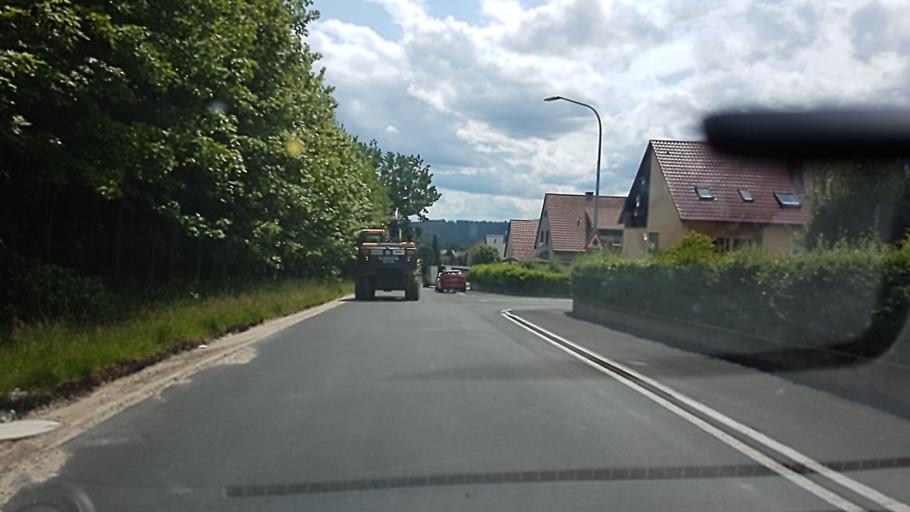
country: DE
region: Bavaria
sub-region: Upper Palatinate
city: Brand
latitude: 49.9709
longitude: 11.9093
